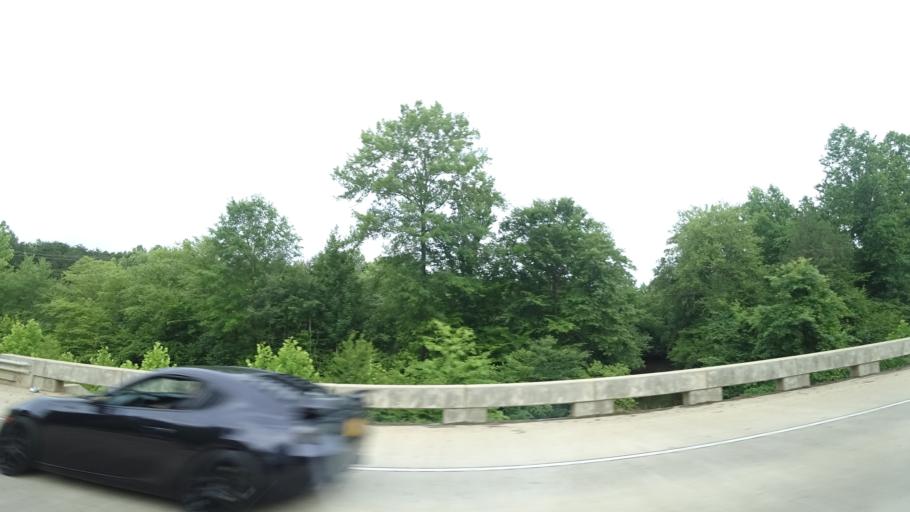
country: US
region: Virginia
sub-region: Spotsylvania County
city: Spotsylvania Courthouse
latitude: 38.1788
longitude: -77.6242
